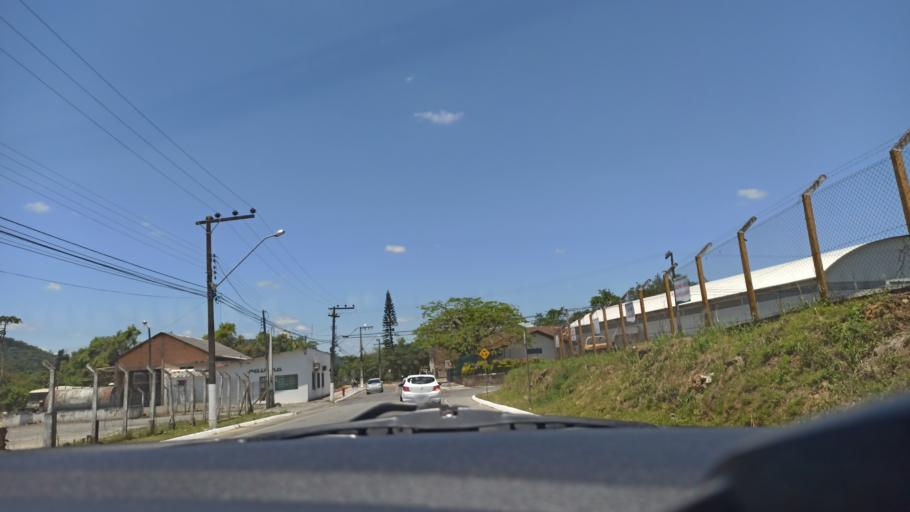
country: BR
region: Santa Catarina
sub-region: Indaial
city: Indaial
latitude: -26.8899
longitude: -49.2380
